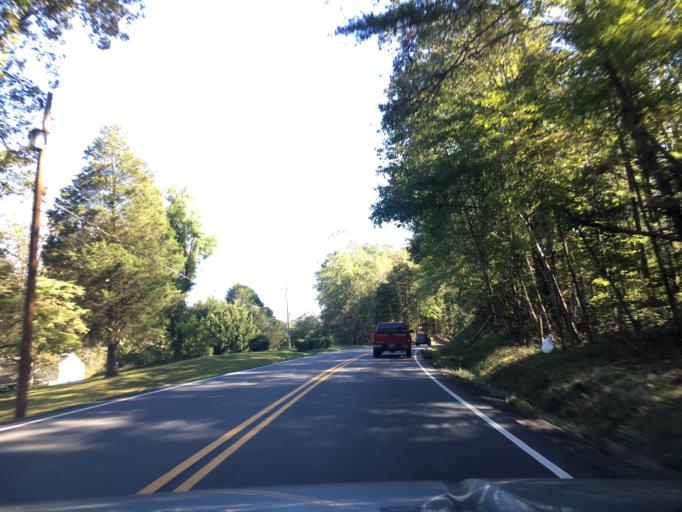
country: US
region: Virginia
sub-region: Goochland County
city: Goochland
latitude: 37.7000
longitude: -77.8386
